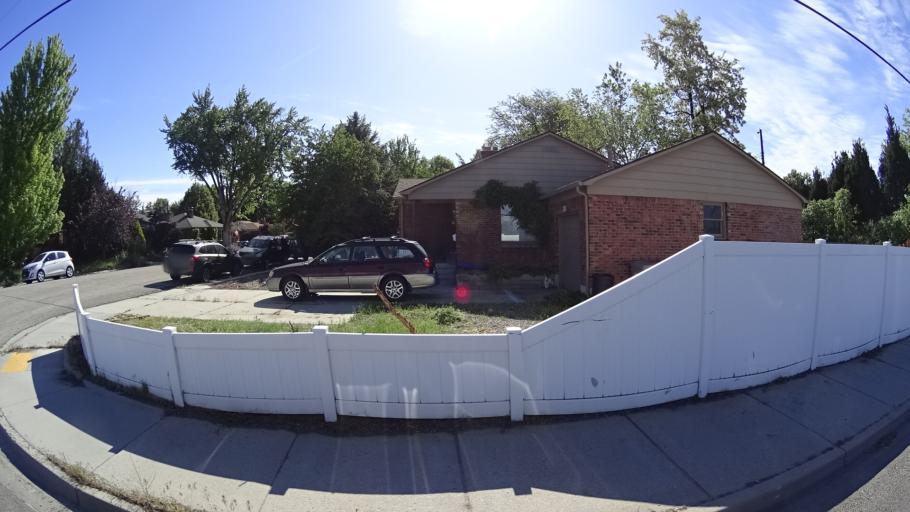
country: US
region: Idaho
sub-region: Ada County
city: Garden City
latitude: 43.5940
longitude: -116.2436
